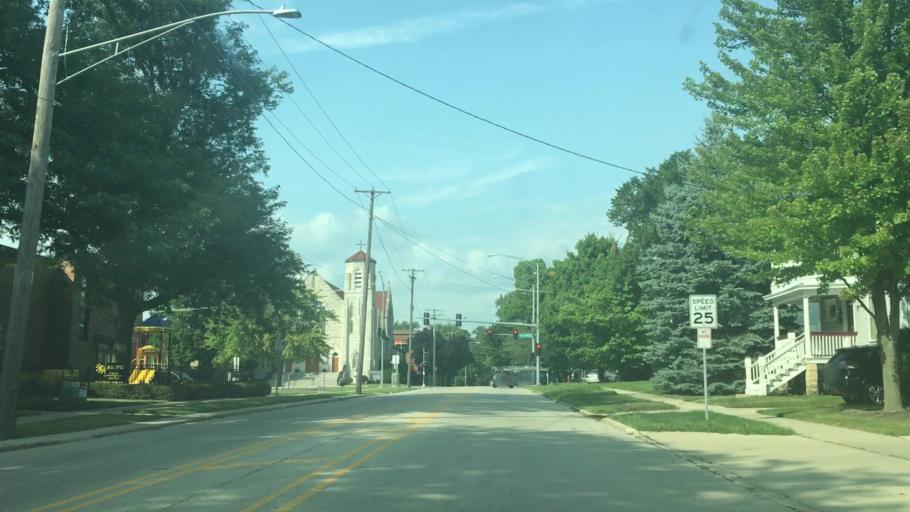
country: US
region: Illinois
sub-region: DeKalb County
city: DeKalb
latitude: 41.9317
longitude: -88.7488
